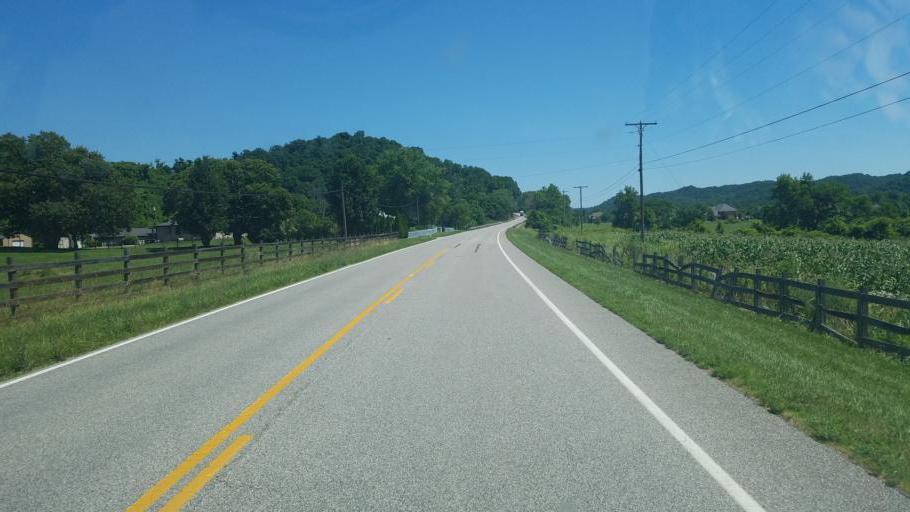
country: US
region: West Virginia
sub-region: Cabell County
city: Lesage
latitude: 38.5460
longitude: -82.2995
